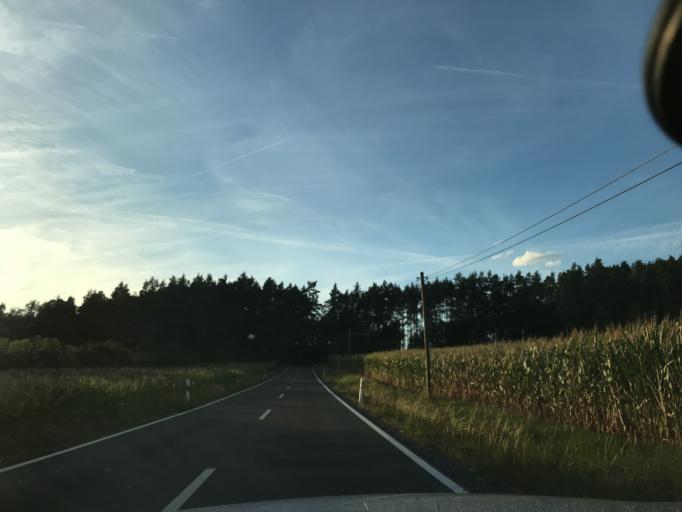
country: DE
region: Bavaria
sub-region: Upper Franconia
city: Pegnitz
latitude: 49.7281
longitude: 11.5586
